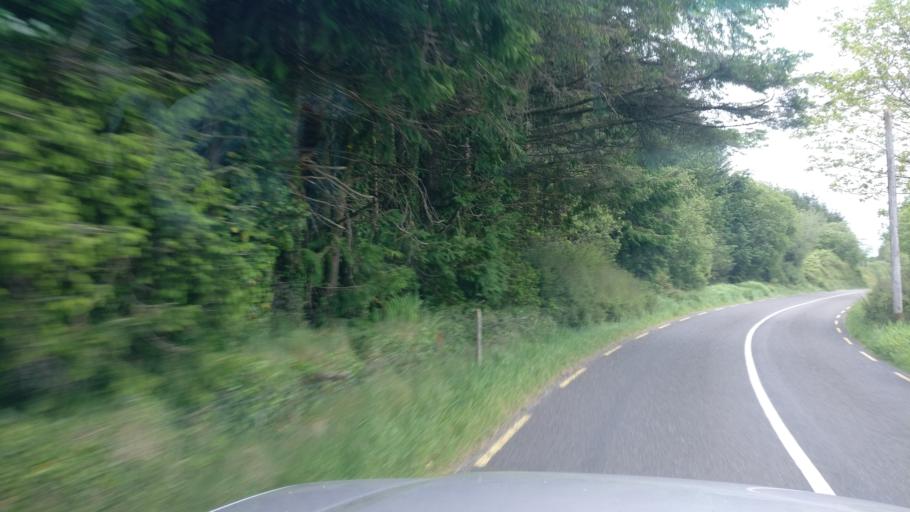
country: IE
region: Connaught
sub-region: County Galway
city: Loughrea
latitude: 53.0717
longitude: -8.5917
